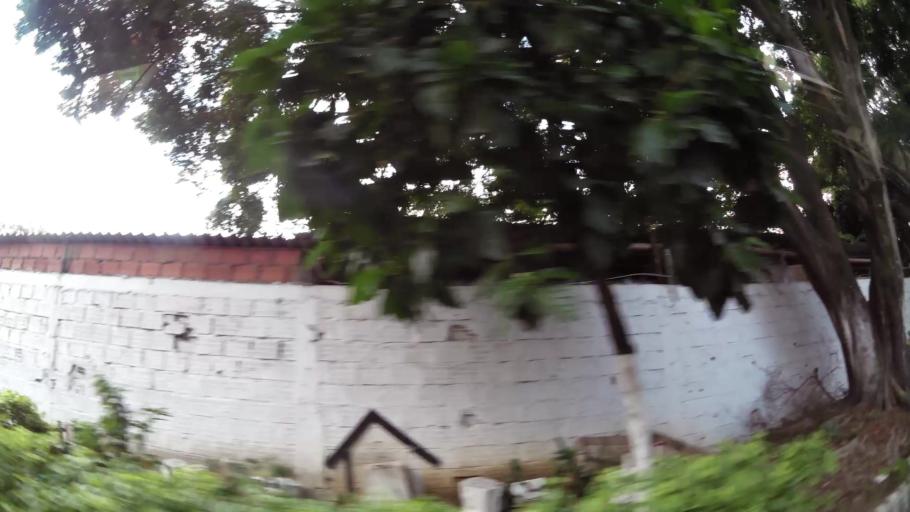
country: CO
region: Valle del Cauca
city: Cali
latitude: 3.4055
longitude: -76.5299
